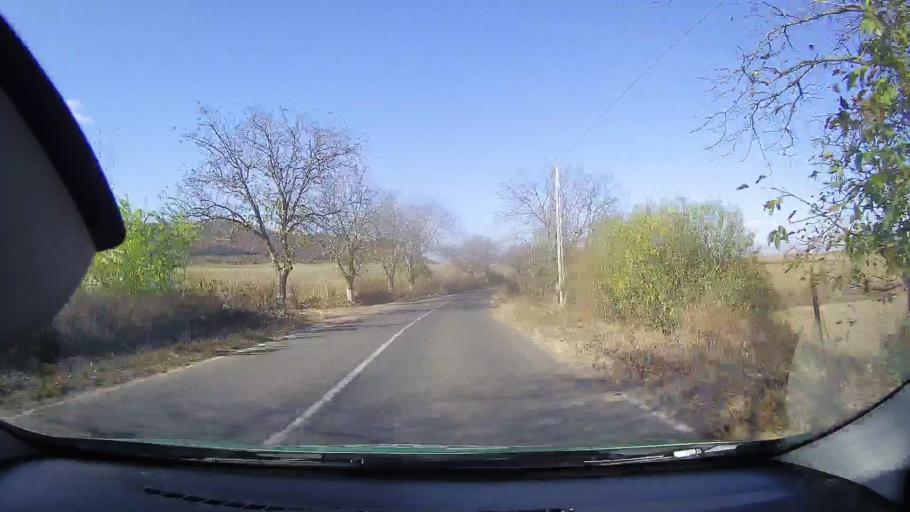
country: RO
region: Tulcea
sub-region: Oras Babadag
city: Babadag
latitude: 44.8804
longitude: 28.7466
